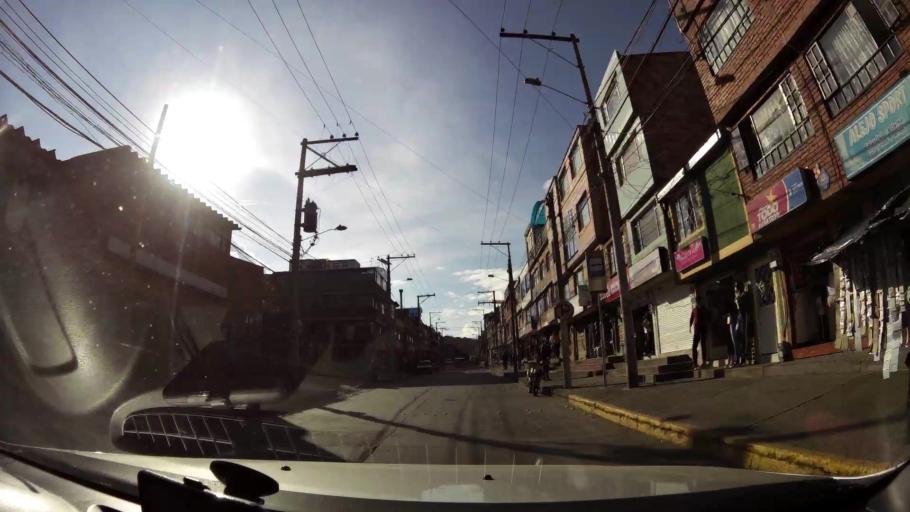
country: CO
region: Cundinamarca
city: Soacha
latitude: 4.5690
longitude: -74.1497
